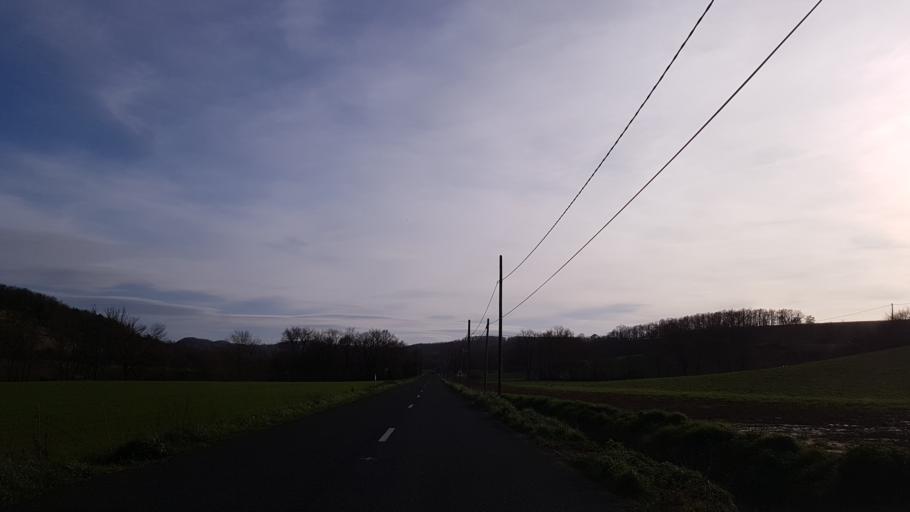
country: FR
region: Midi-Pyrenees
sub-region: Departement de l'Ariege
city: Mirepoix
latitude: 43.1729
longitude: 1.9124
